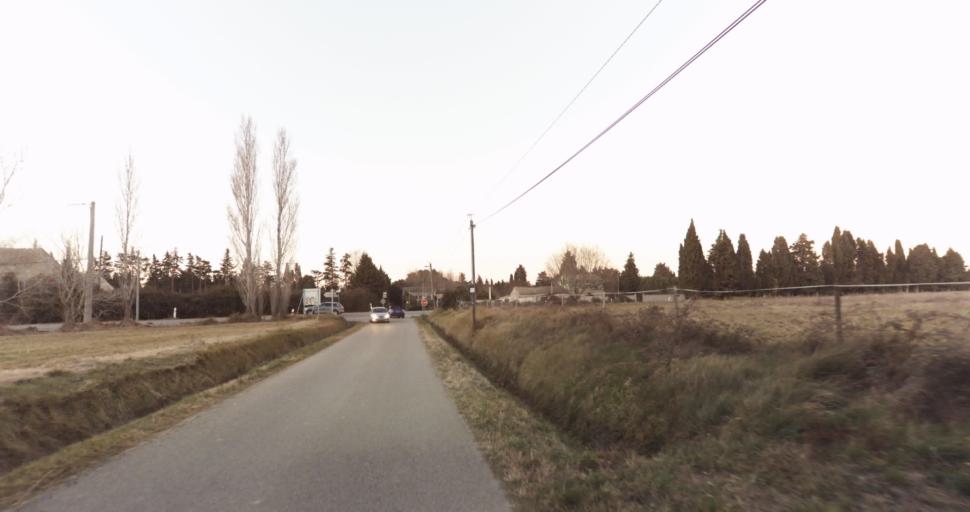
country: FR
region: Provence-Alpes-Cote d'Azur
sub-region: Departement des Bouches-du-Rhone
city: Barbentane
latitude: 43.9068
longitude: 4.7762
